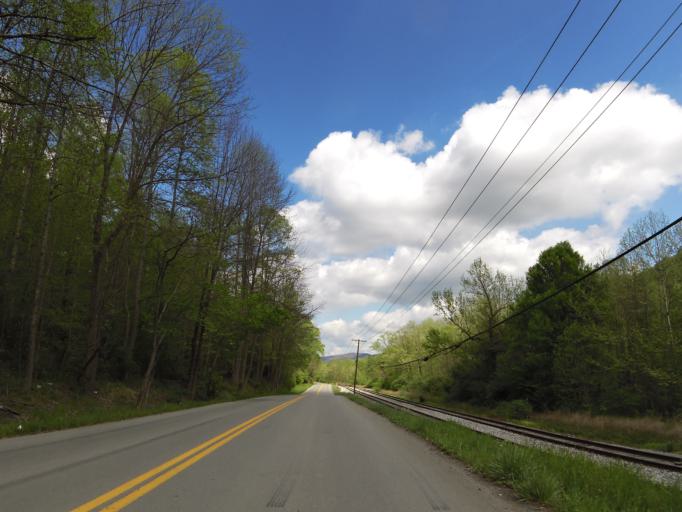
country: US
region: Kentucky
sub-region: Bell County
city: Middlesboro
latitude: 36.6142
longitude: -83.7745
